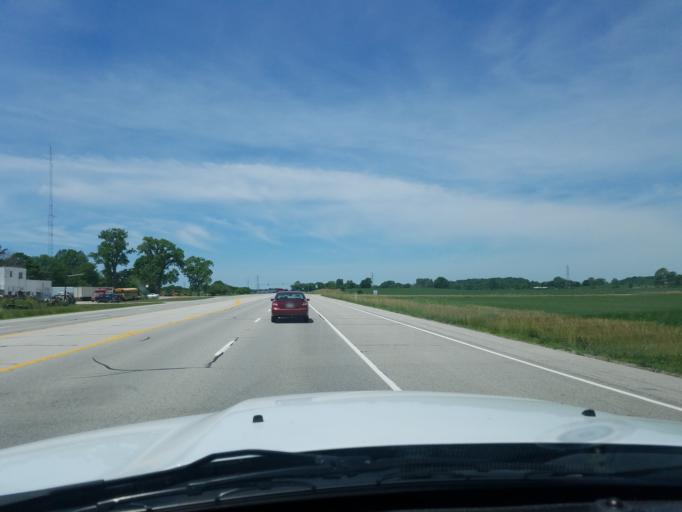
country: US
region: Indiana
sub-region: Delaware County
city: Daleville
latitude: 40.1137
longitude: -85.5168
